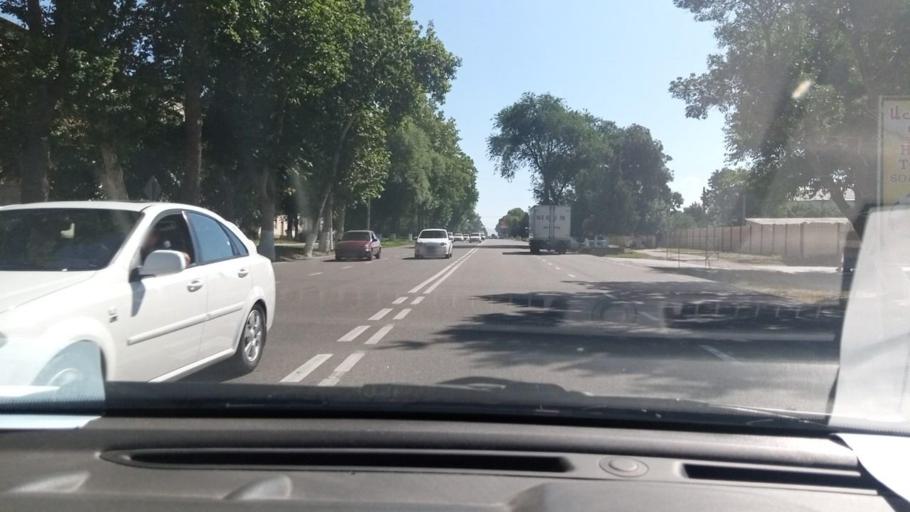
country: UZ
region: Toshkent
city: Angren
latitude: 41.0008
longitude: 70.0769
